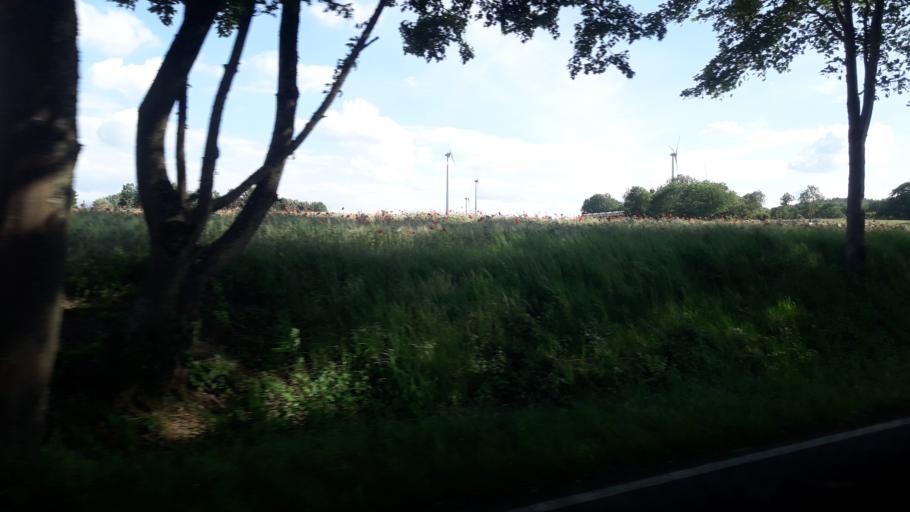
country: DE
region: North Rhine-Westphalia
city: Lichtenau
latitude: 51.6509
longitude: 8.8718
